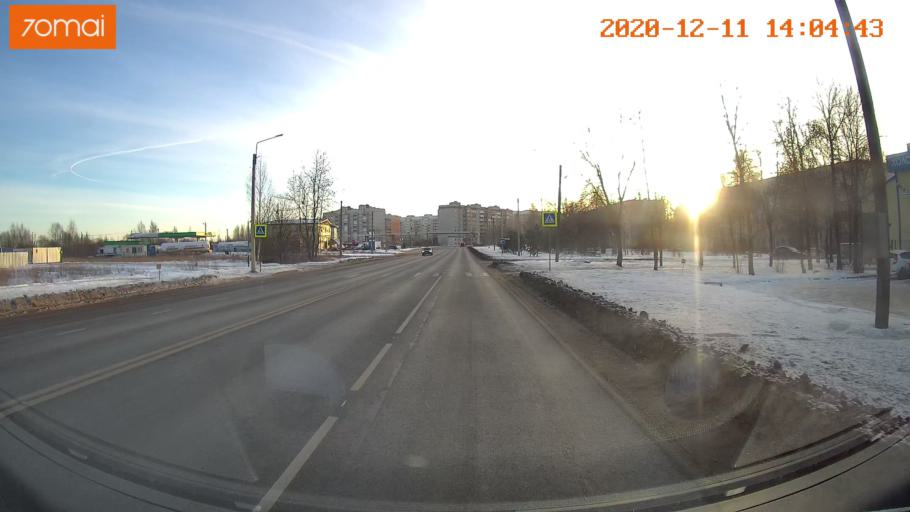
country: RU
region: Kostroma
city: Oktyabr'skiy
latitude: 57.7527
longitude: 41.0163
